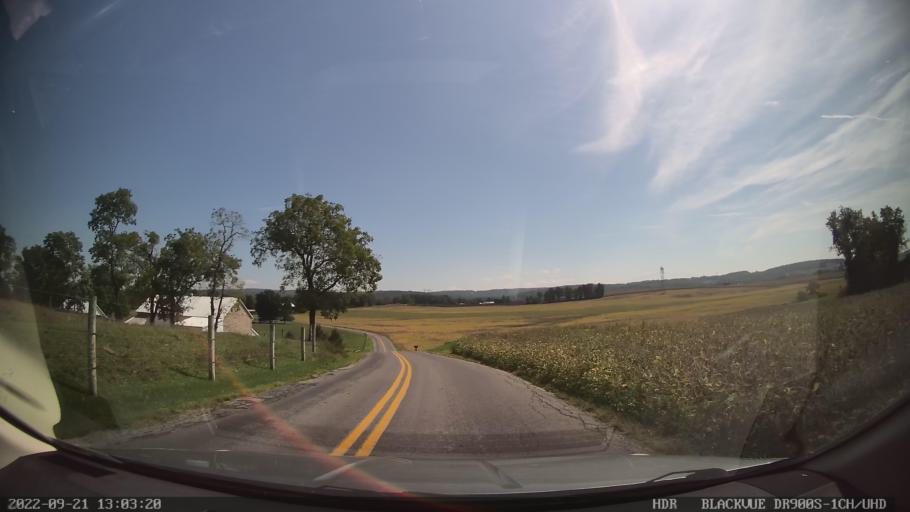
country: US
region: Pennsylvania
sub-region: Berks County
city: Kutztown
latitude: 40.4959
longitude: -75.7558
